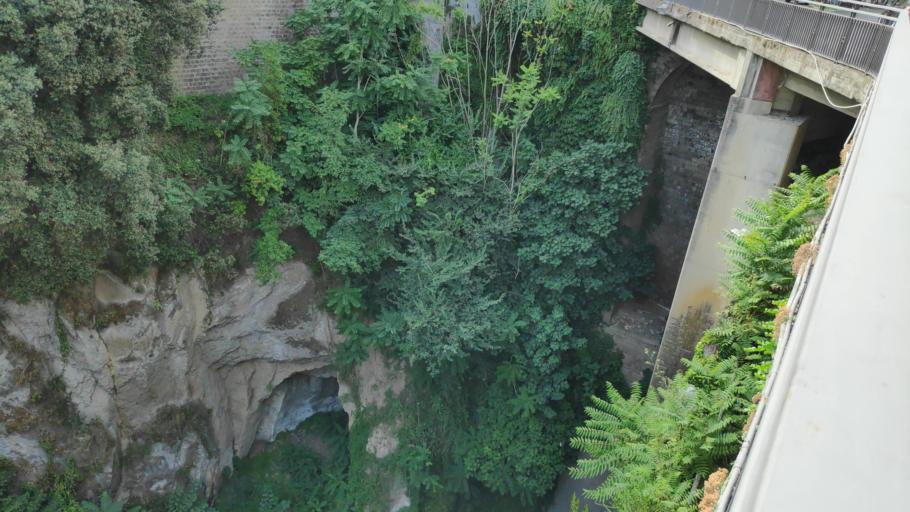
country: IT
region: Campania
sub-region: Provincia di Napoli
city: Sorrento
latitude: 40.6251
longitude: 14.3766
